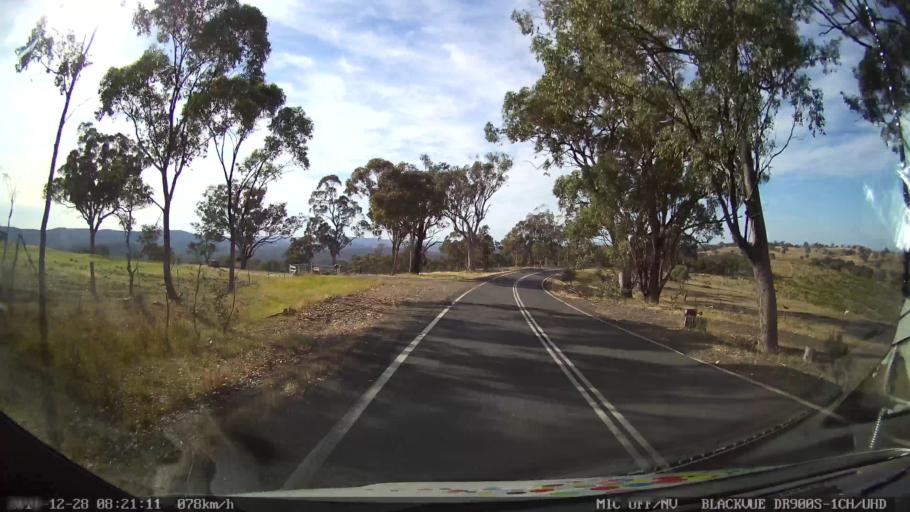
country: AU
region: New South Wales
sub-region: Blayney
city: Blayney
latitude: -33.8798
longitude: 149.3506
